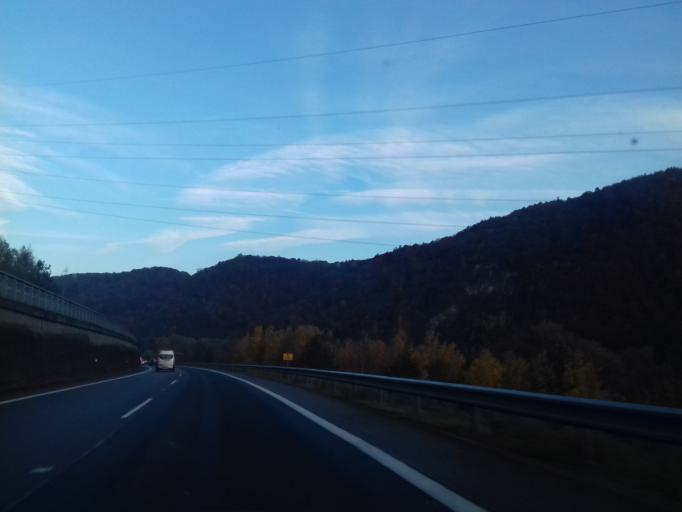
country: SK
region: Banskobystricky
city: Ziar nad Hronom
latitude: 48.5787
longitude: 18.9842
